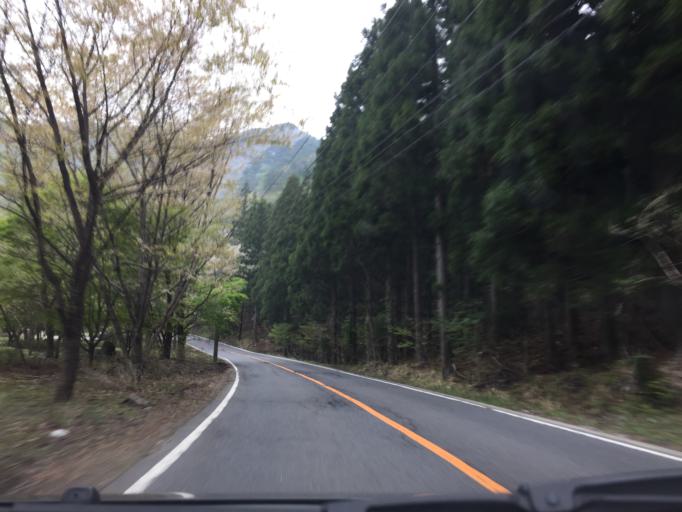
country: JP
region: Tochigi
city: Nikko
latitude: 36.9586
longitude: 139.6971
